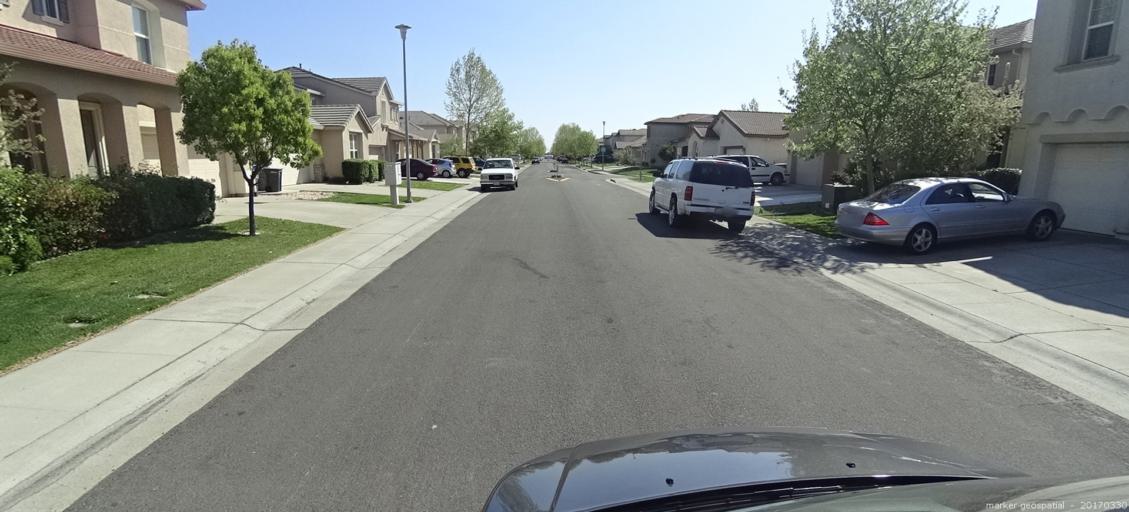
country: US
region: California
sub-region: Sacramento County
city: Laguna
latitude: 38.4420
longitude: -121.4140
